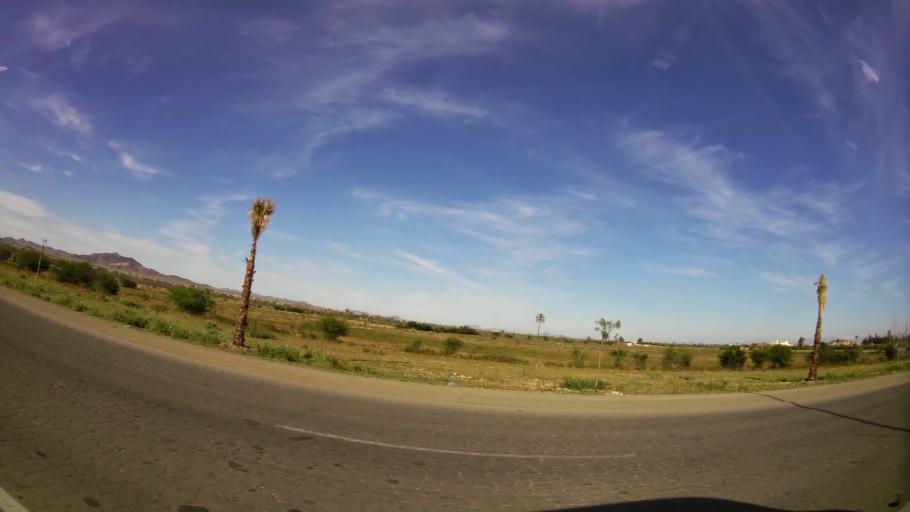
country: MA
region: Marrakech-Tensift-Al Haouz
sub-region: Marrakech
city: Marrakesh
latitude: 31.6860
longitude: -8.0522
